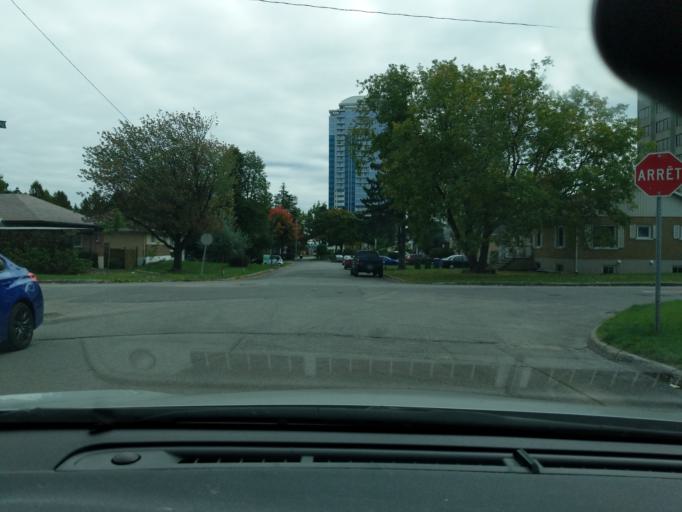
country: CA
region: Quebec
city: L'Ancienne-Lorette
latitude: 46.7705
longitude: -71.2915
